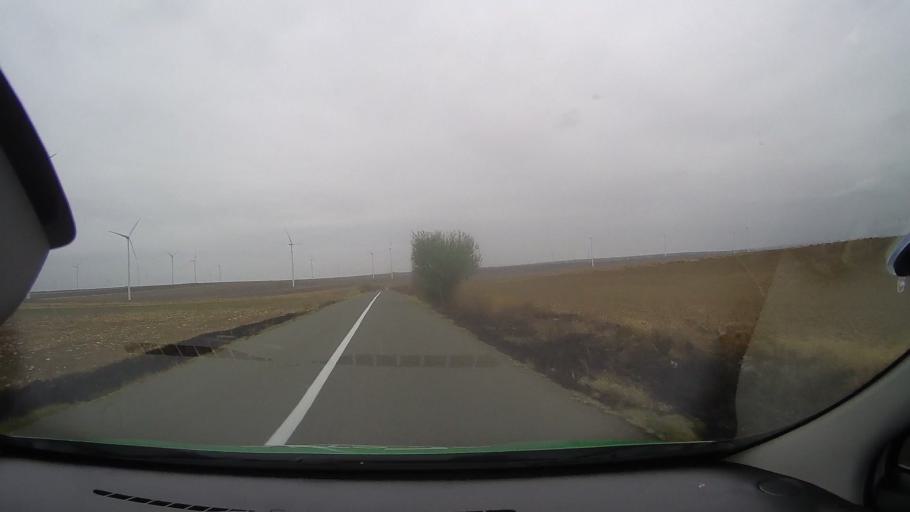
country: RO
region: Constanta
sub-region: Comuna Pantelimon
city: Pantelimon
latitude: 44.5100
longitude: 28.3398
